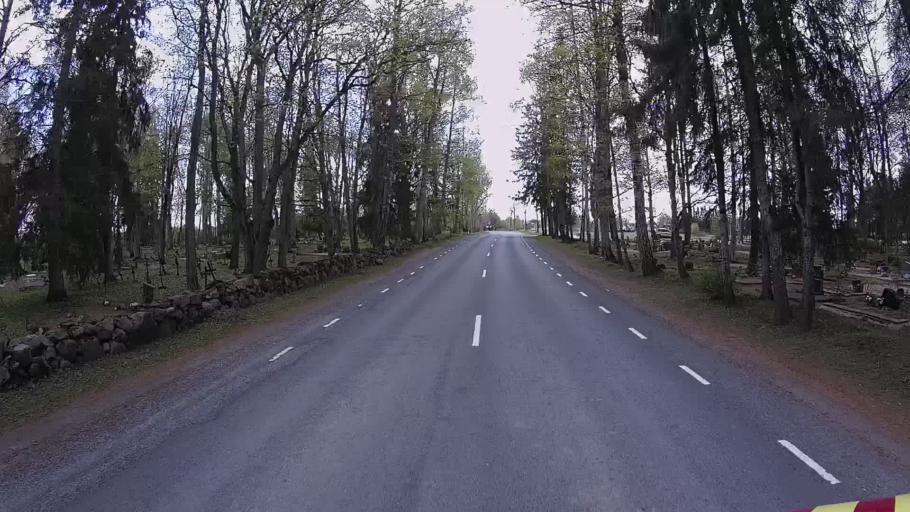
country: EE
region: Jaervamaa
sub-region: Koeru vald
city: Koeru
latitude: 58.9699
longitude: 26.0336
